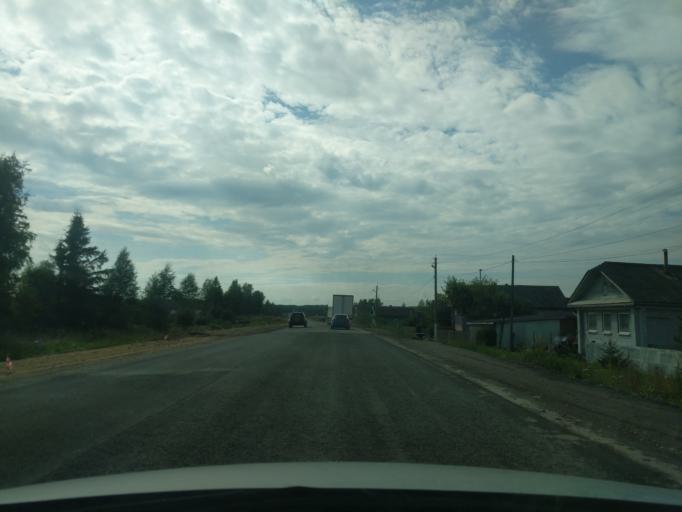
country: RU
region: Kostroma
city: Sudislavl'
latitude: 57.8617
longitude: 41.6185
